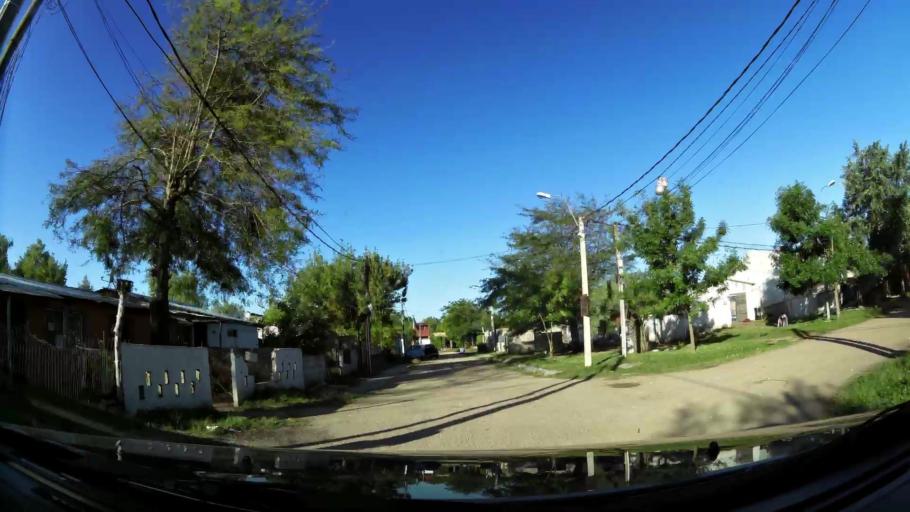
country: UY
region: Canelones
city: Paso de Carrasco
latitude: -34.8497
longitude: -56.0494
